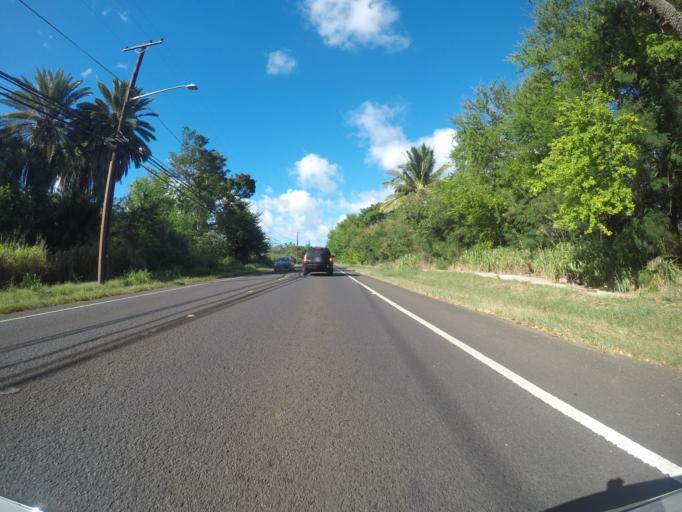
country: US
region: Hawaii
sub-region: Honolulu County
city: Hale'iwa
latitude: 21.6108
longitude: -158.0932
